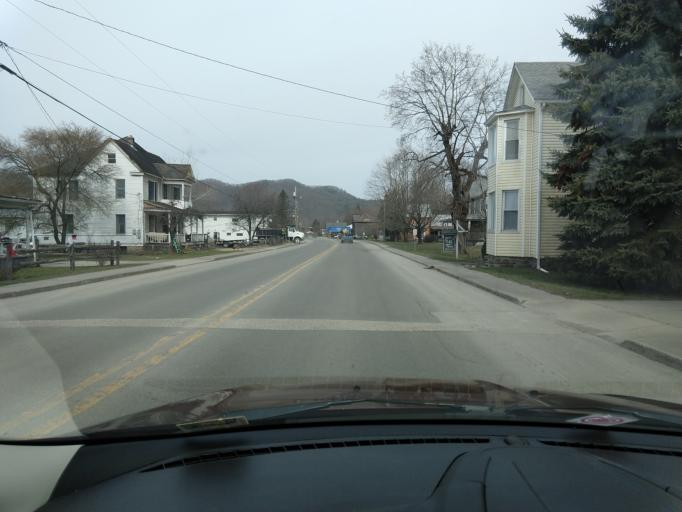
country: US
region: West Virginia
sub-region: Tucker County
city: Parsons
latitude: 39.0975
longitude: -79.6721
